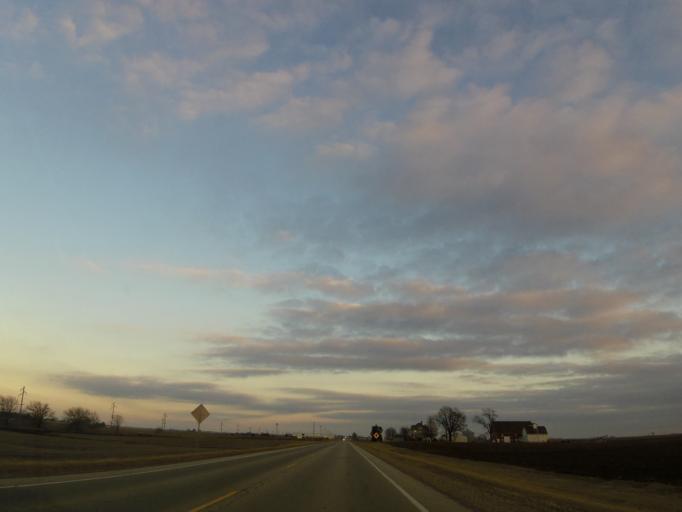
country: US
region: Illinois
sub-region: Woodford County
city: El Paso
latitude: 40.7378
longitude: -88.9901
